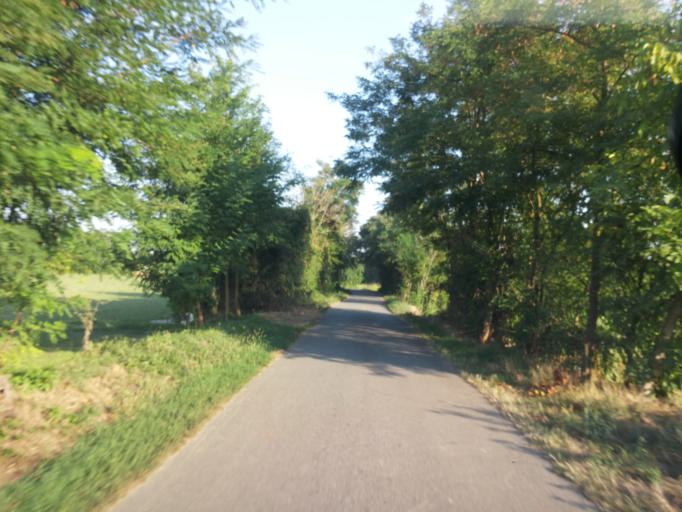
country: IT
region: Piedmont
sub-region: Provincia di Biella
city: Cavaglia
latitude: 45.4003
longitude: 8.1014
